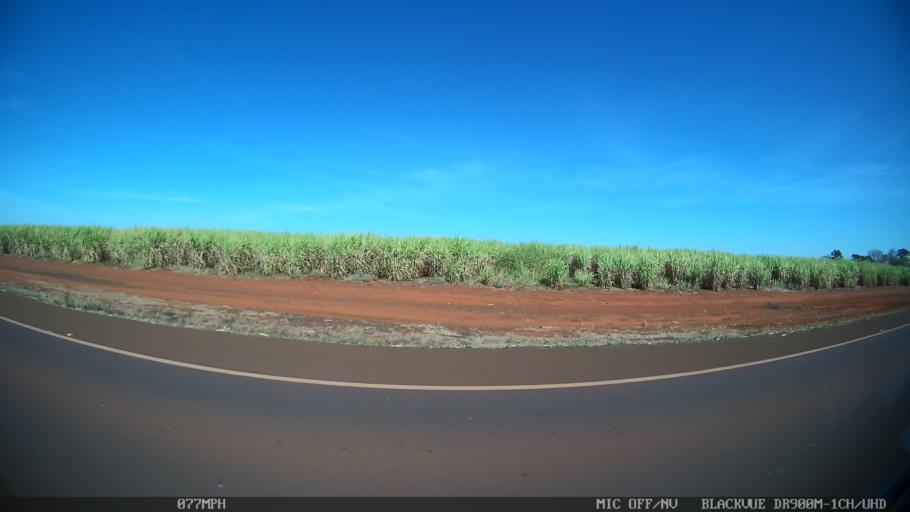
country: BR
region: Sao Paulo
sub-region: Guaira
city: Guaira
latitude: -20.4440
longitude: -48.2974
